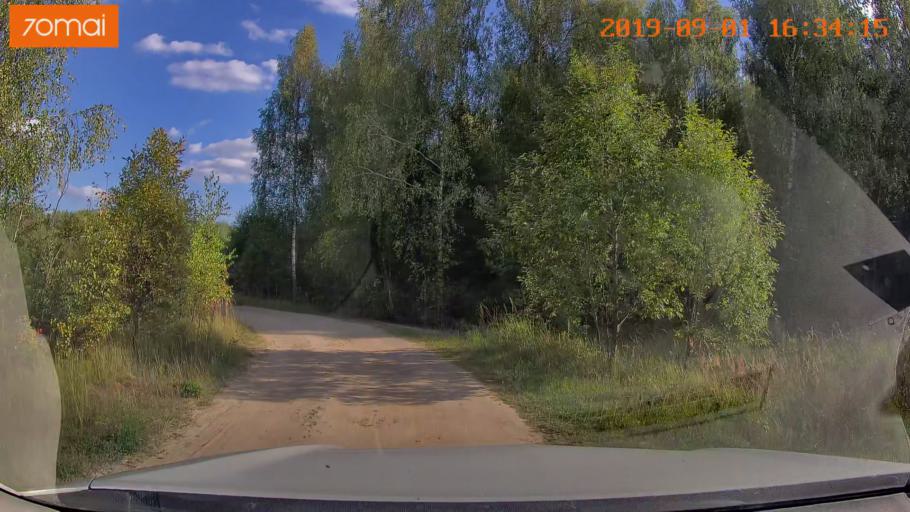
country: RU
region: Kaluga
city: Maloyaroslavets
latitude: 54.9482
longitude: 36.4752
